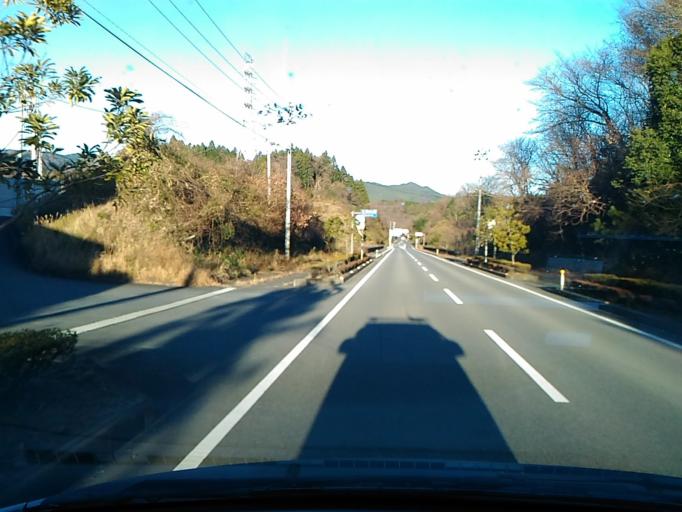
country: JP
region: Ibaraki
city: Kitaibaraki
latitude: 36.9069
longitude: 140.7501
